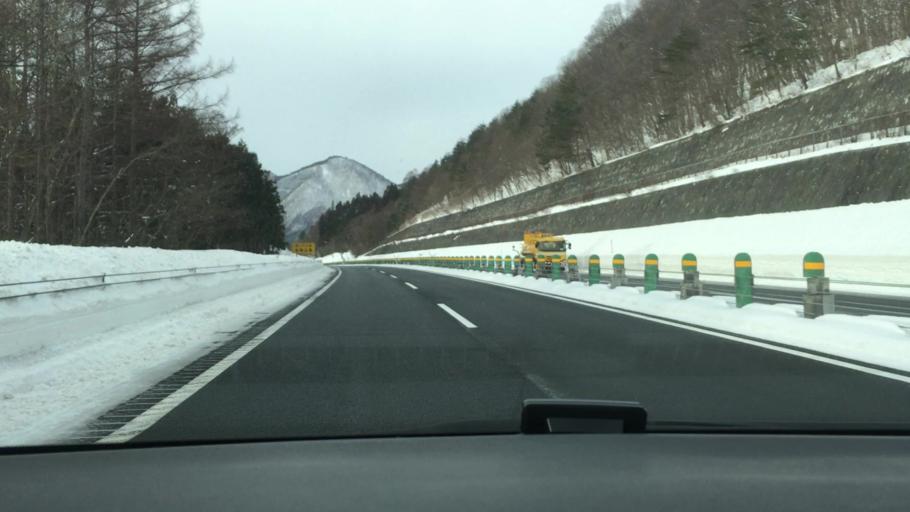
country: JP
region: Akita
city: Hanawa
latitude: 40.1366
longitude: 140.9689
